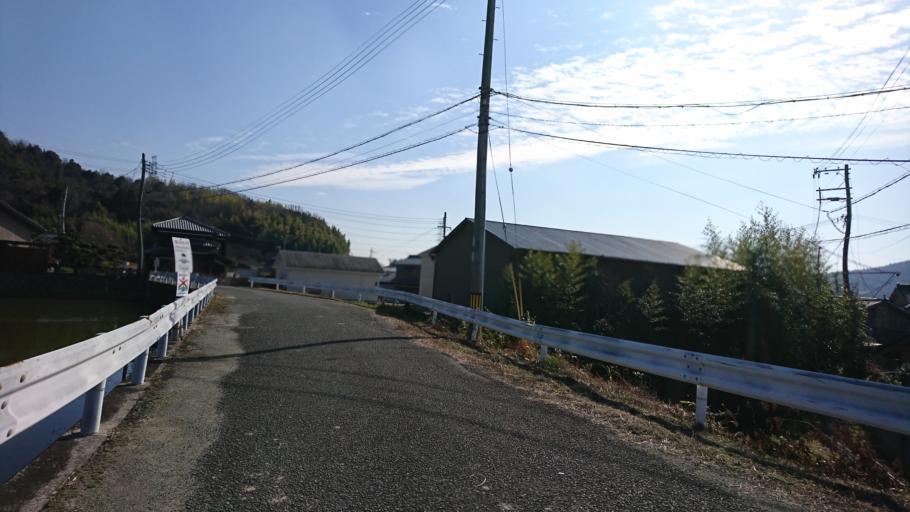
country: JP
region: Hyogo
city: Kakogawacho-honmachi
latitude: 34.8175
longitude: 134.8548
